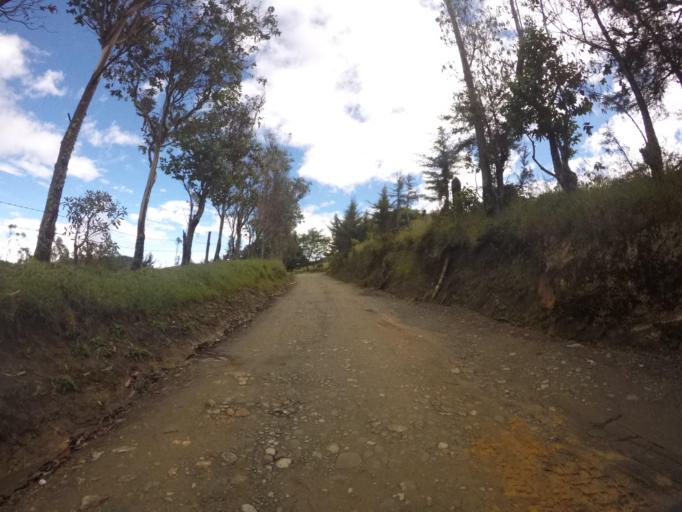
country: CO
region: Cauca
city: Silvia
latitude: 2.6829
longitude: -76.3443
